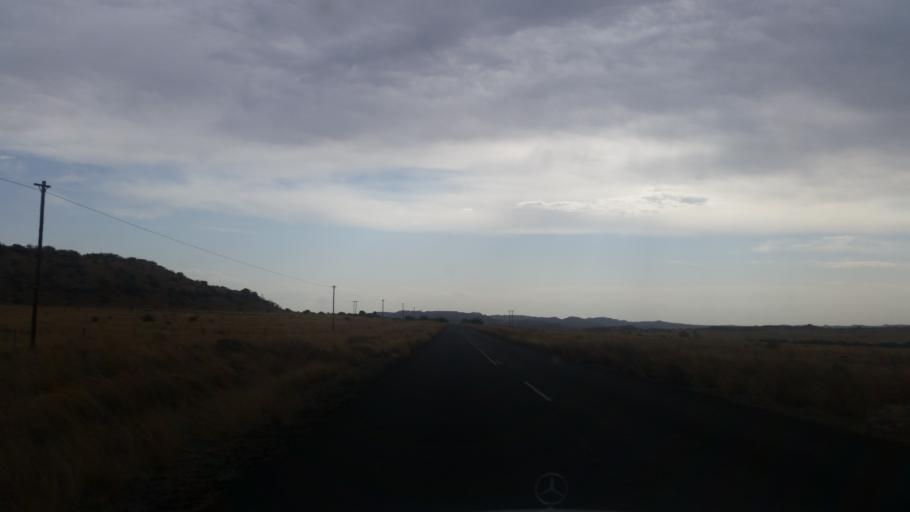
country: ZA
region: Orange Free State
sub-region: Xhariep District Municipality
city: Trompsburg
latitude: -30.4225
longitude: 26.1613
